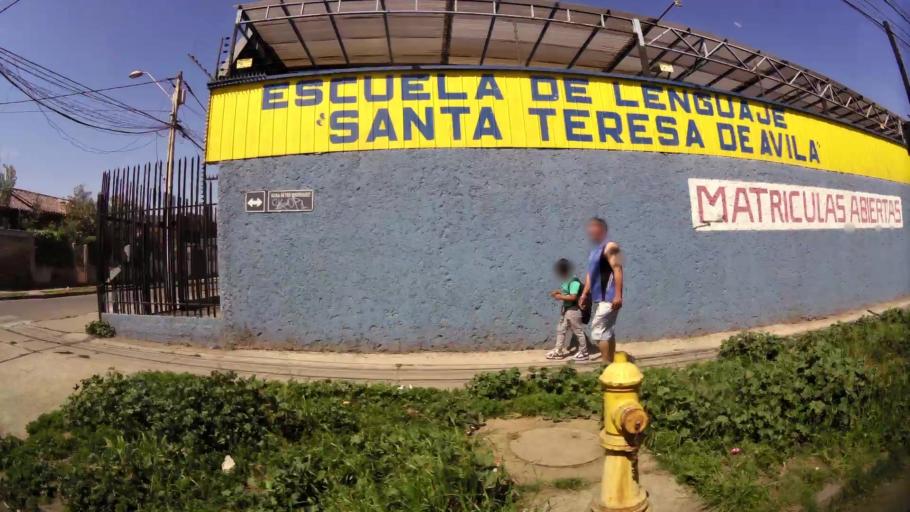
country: CL
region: Santiago Metropolitan
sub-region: Provincia de Santiago
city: Lo Prado
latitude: -33.4898
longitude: -70.7250
